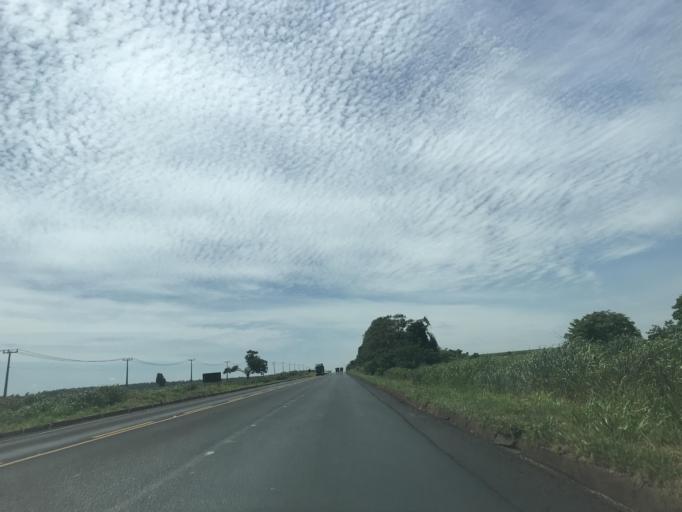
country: BR
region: Parana
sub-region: Paranavai
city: Paranavai
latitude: -23.0015
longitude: -52.5603
